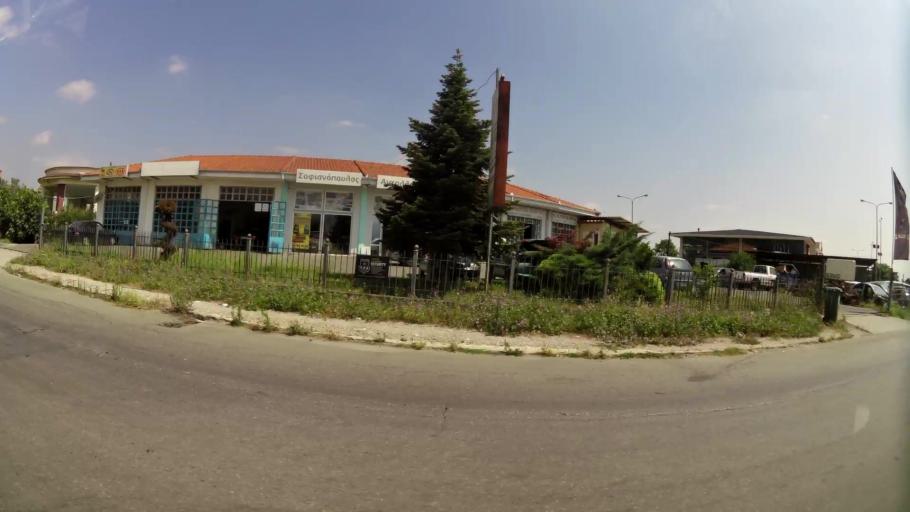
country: GR
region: Central Macedonia
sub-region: Nomos Imathias
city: Veroia
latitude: 40.5280
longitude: 22.2104
